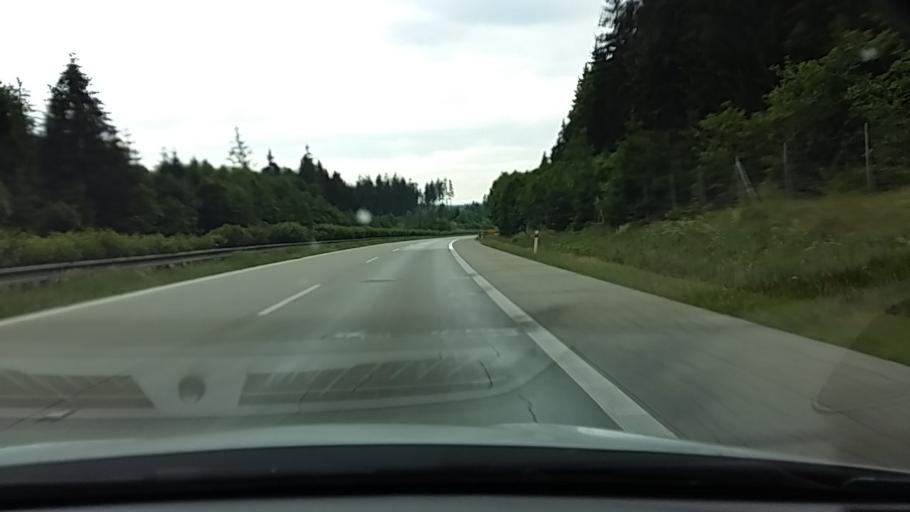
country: CZ
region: Plzensky
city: Primda
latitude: 49.6847
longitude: 12.6519
